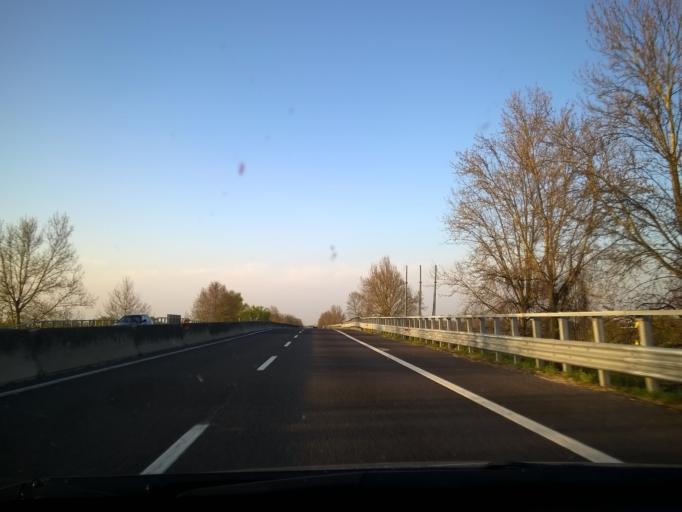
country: IT
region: Emilia-Romagna
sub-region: Provincia di Ferrara
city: Porotto-Cassama
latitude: 44.8425
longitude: 11.5643
